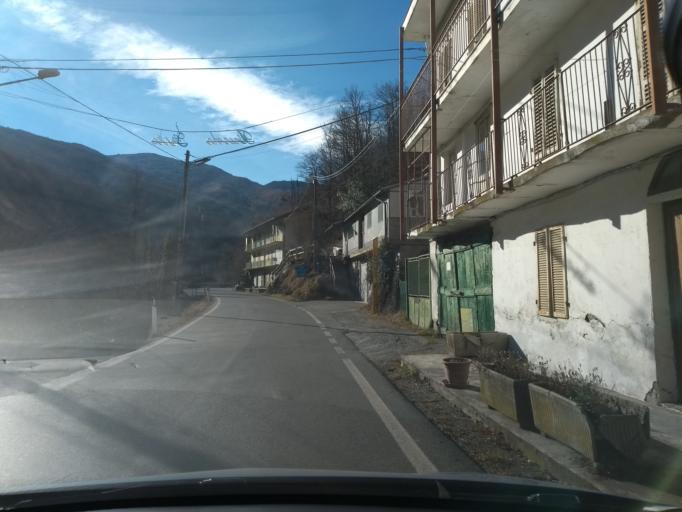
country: IT
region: Piedmont
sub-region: Provincia di Torino
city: La Villa
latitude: 45.2394
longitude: 7.4370
